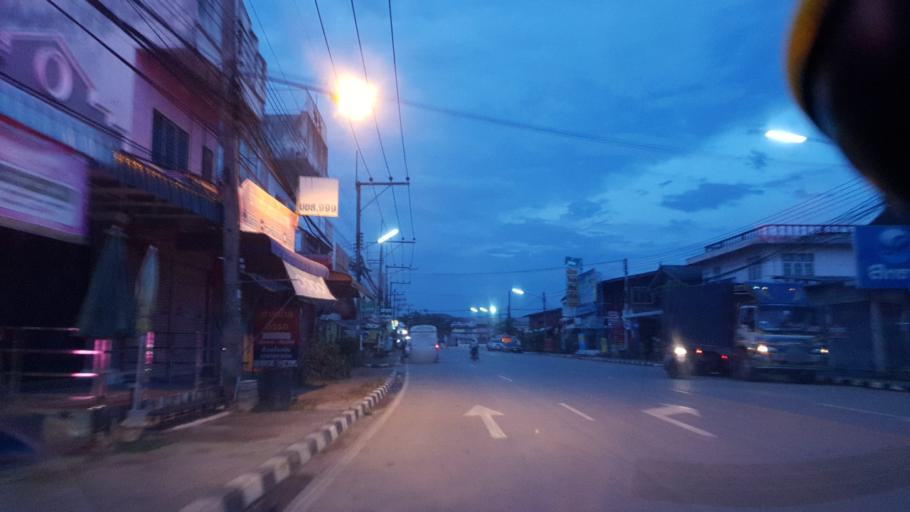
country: TH
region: Chiang Rai
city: Wiang Chiang Rung
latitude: 20.0042
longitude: 100.0415
